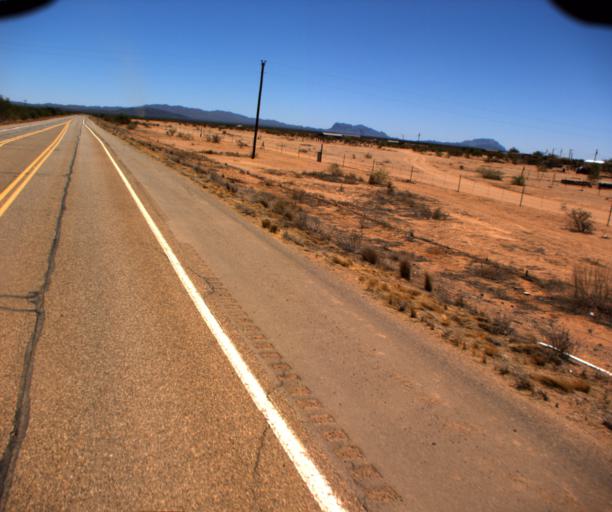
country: US
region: Arizona
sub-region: Pima County
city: Ajo
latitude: 32.1848
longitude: -112.3667
